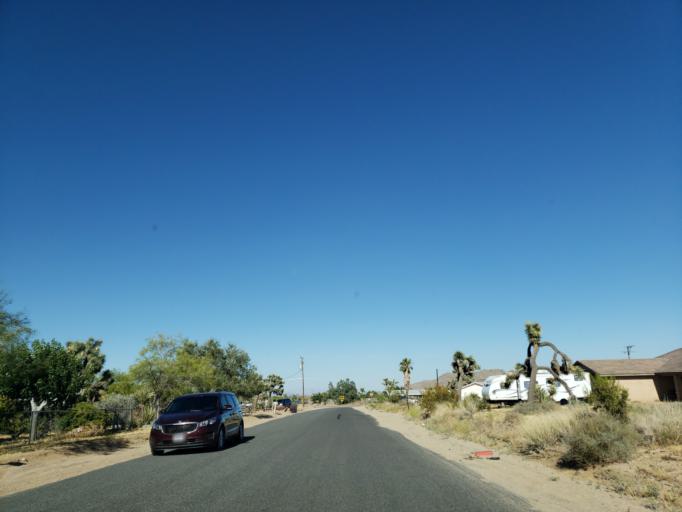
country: US
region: California
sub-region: San Bernardino County
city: Yucca Valley
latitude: 34.1838
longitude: -116.3886
